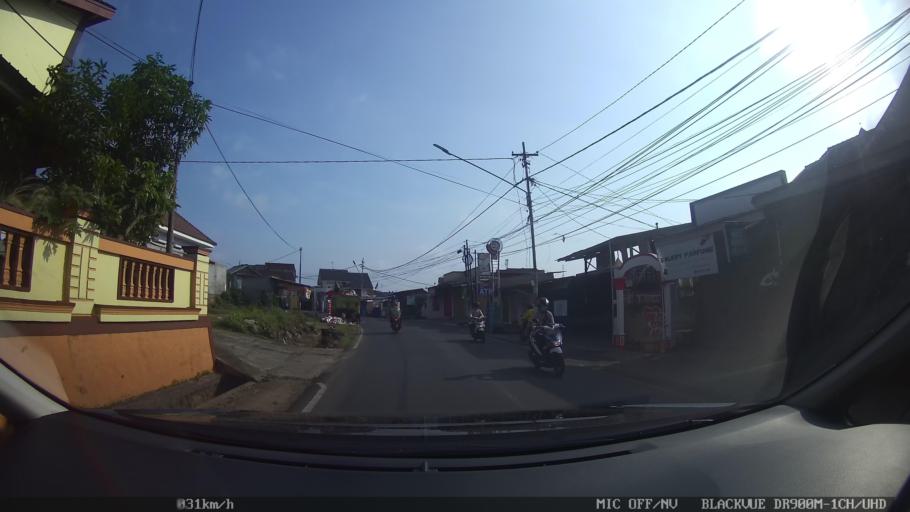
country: ID
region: Lampung
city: Kedaton
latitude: -5.4003
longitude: 105.2487
